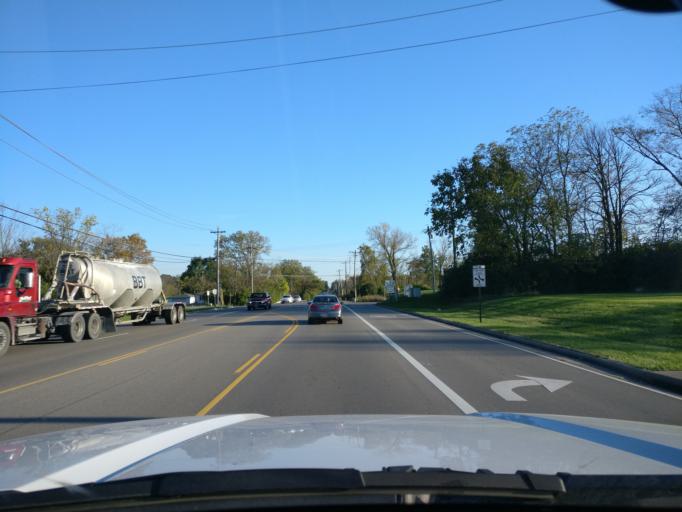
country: US
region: Ohio
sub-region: Warren County
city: Franklin
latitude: 39.5366
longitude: -84.2877
